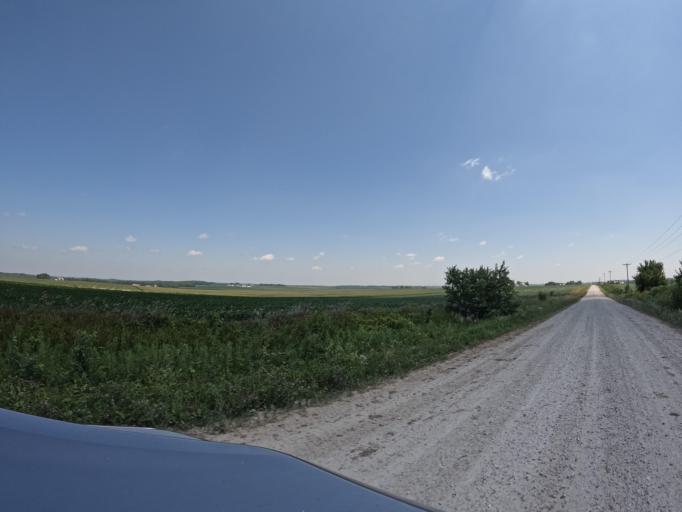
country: US
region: Iowa
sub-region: Keokuk County
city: Sigourney
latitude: 41.2795
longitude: -92.2296
